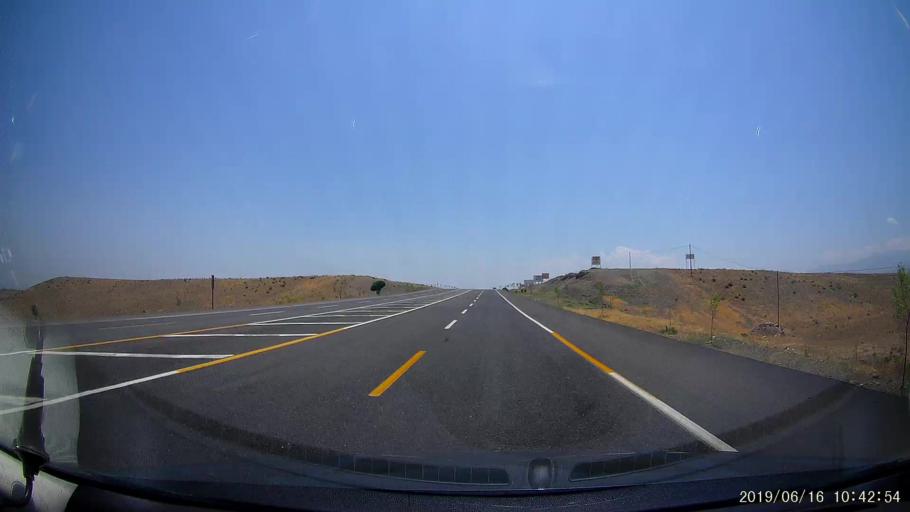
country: AM
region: Armavir
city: Shenavan
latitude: 40.0387
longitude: 43.8160
